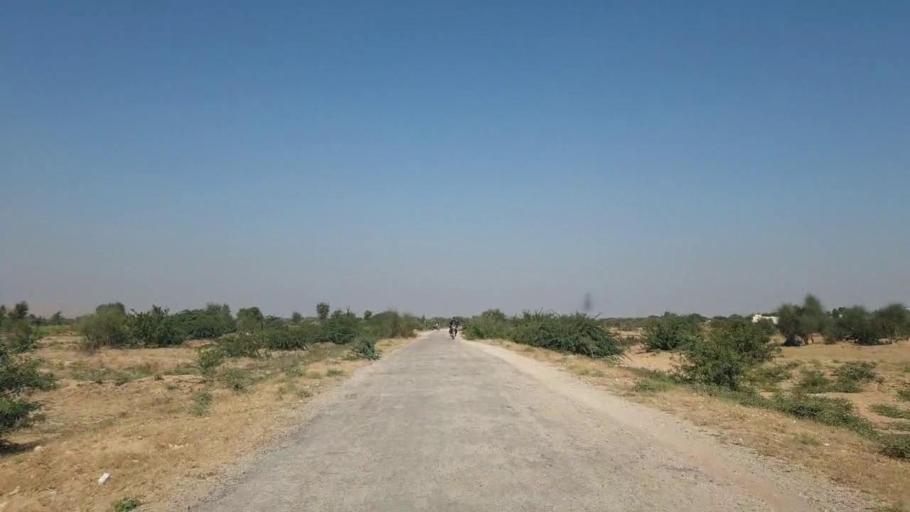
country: PK
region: Sindh
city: Jamshoro
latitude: 25.3754
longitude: 67.8421
